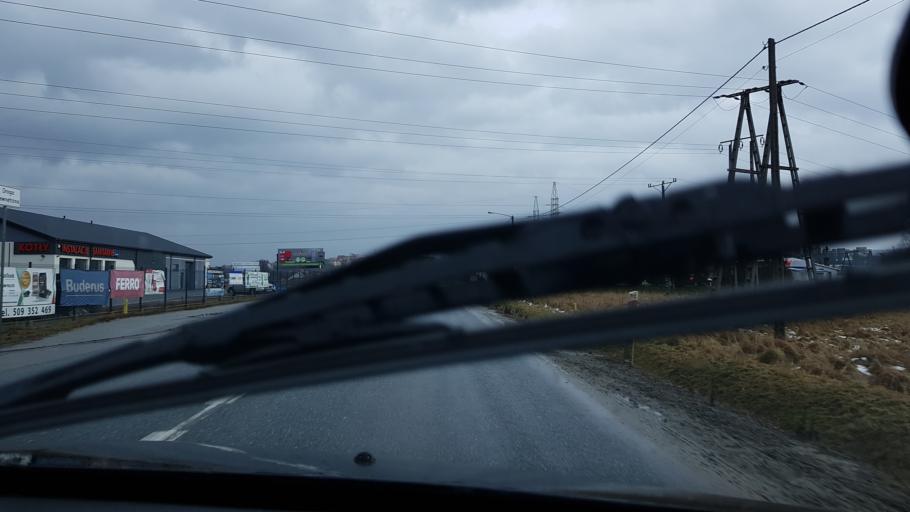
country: PL
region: Lesser Poland Voivodeship
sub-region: Powiat suski
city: Jordanow
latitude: 49.6555
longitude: 19.8142
